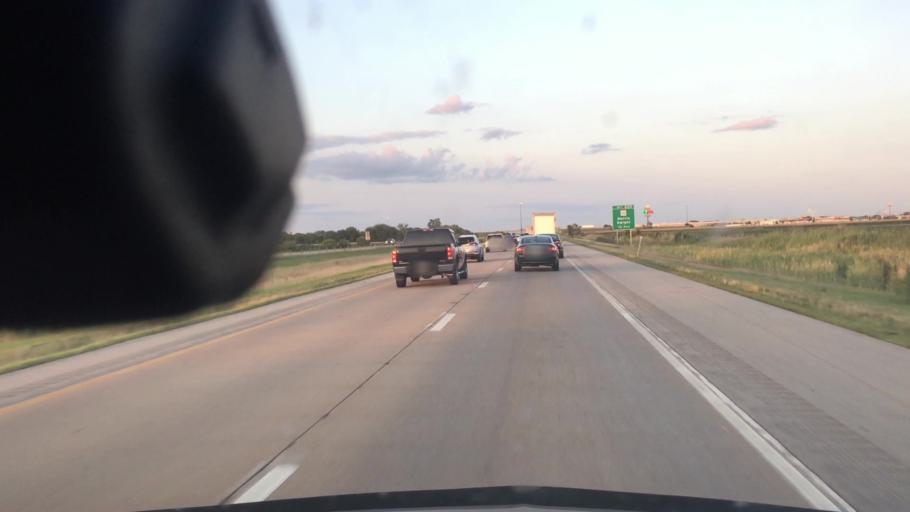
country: US
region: Illinois
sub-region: Livingston County
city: Dwight
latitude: 41.1144
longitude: -88.4301
